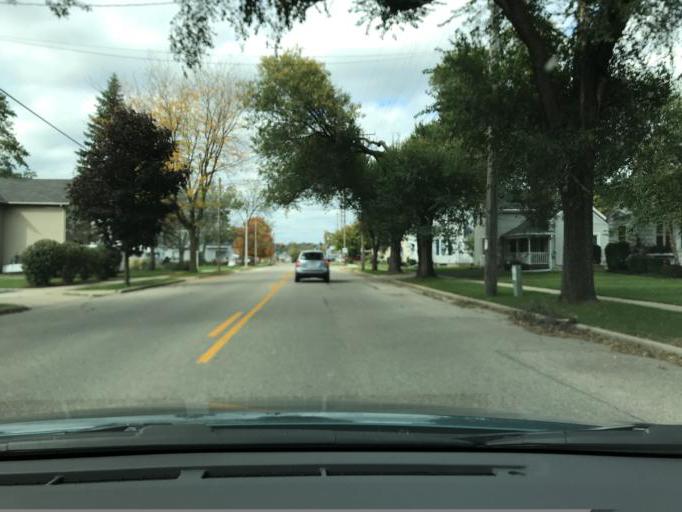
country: US
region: Wisconsin
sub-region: Racine County
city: Burlington
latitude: 42.6768
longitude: -88.2684
